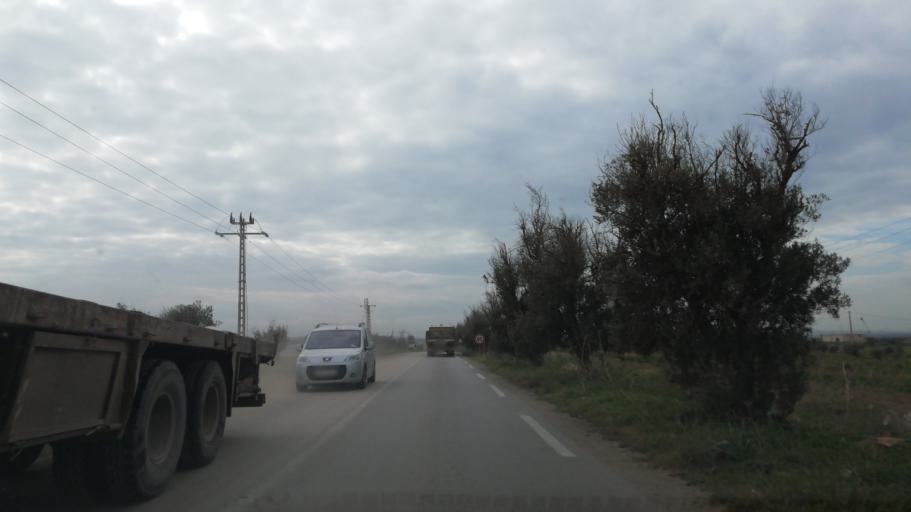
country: DZ
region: Oran
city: Ain el Bya
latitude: 35.7856
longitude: -0.3435
